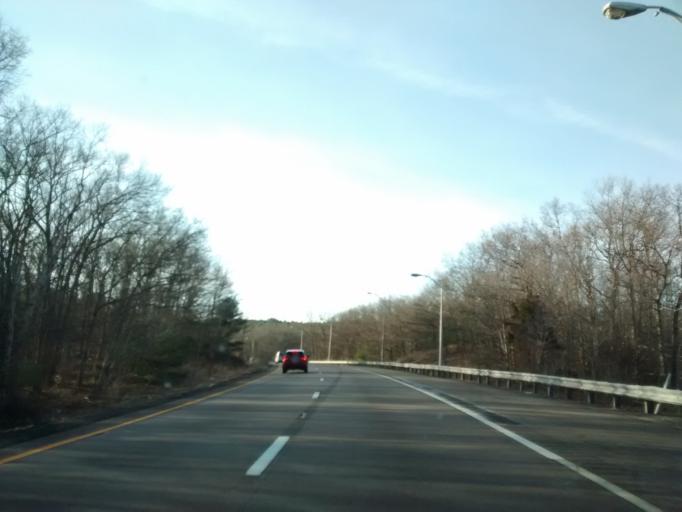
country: US
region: Massachusetts
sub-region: Norfolk County
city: Milton
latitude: 42.1995
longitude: -71.0779
